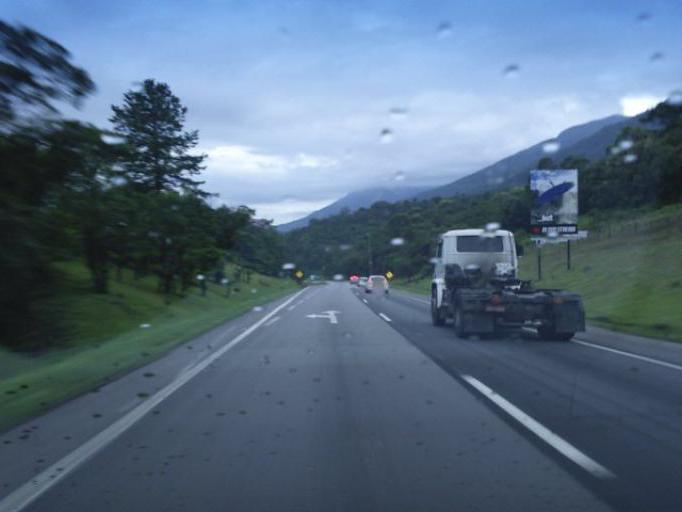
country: BR
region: Parana
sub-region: Guaratuba
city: Guaratuba
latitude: -25.9302
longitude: -48.9123
